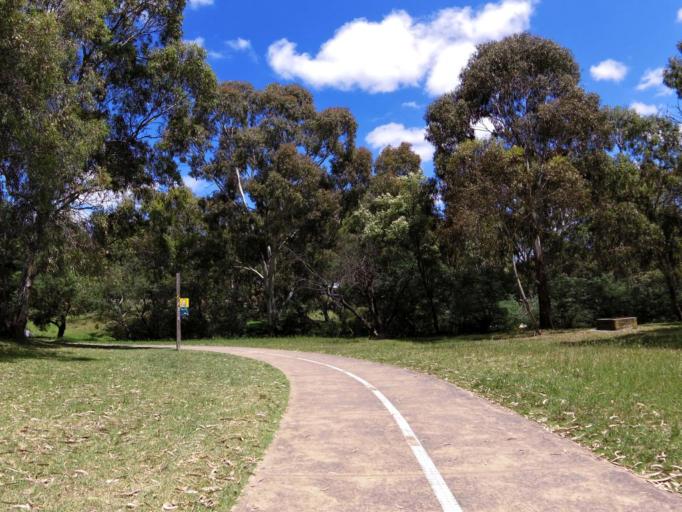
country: AU
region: Victoria
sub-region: Moreland
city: Coburg North
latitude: -37.7341
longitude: 144.9764
